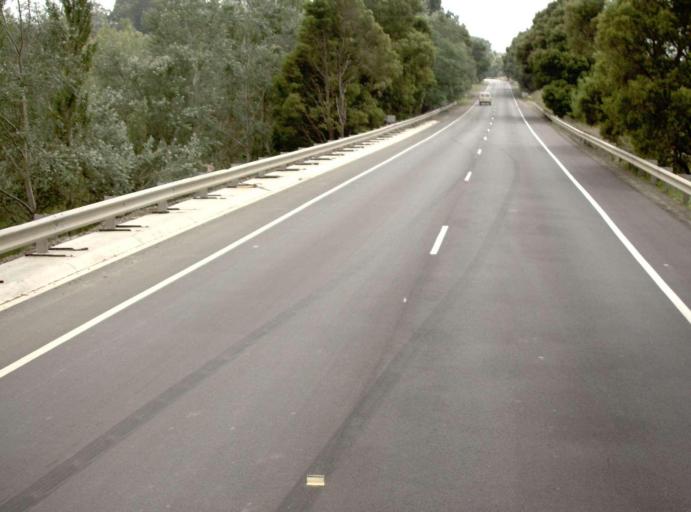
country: AU
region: Victoria
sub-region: Latrobe
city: Moe
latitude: -38.3934
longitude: 146.1193
